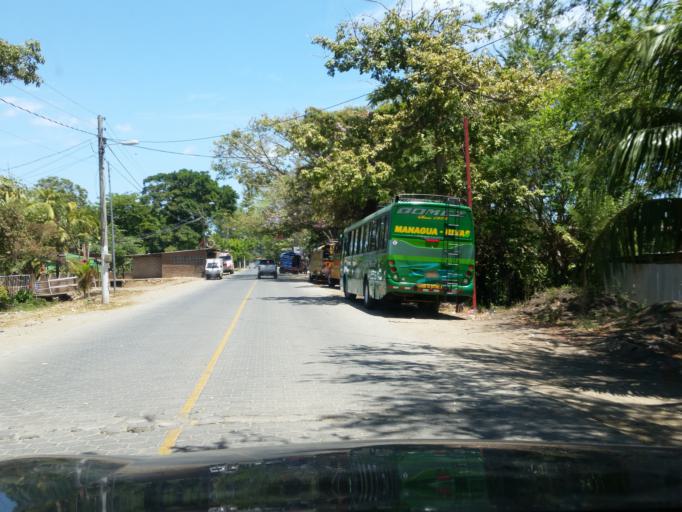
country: NI
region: Rivas
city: Rivas
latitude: 11.4419
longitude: -85.8346
